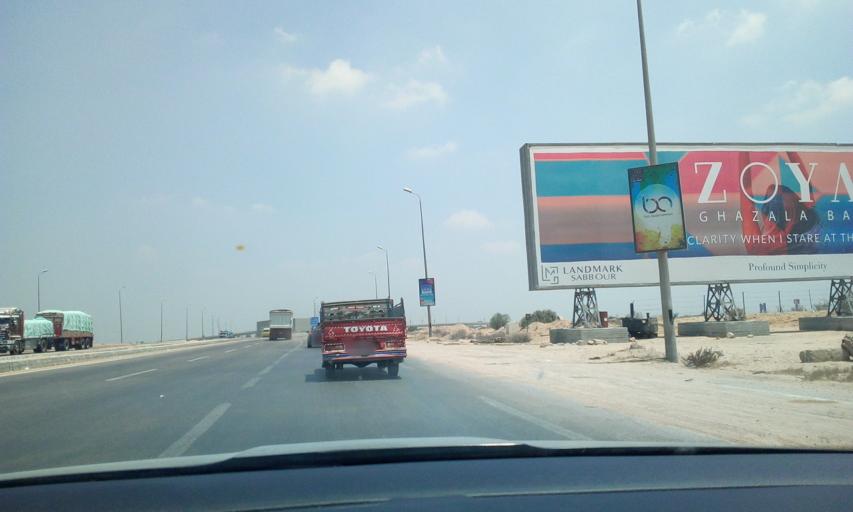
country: EG
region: Al Buhayrah
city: Beheira
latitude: 30.5177
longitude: 30.2266
